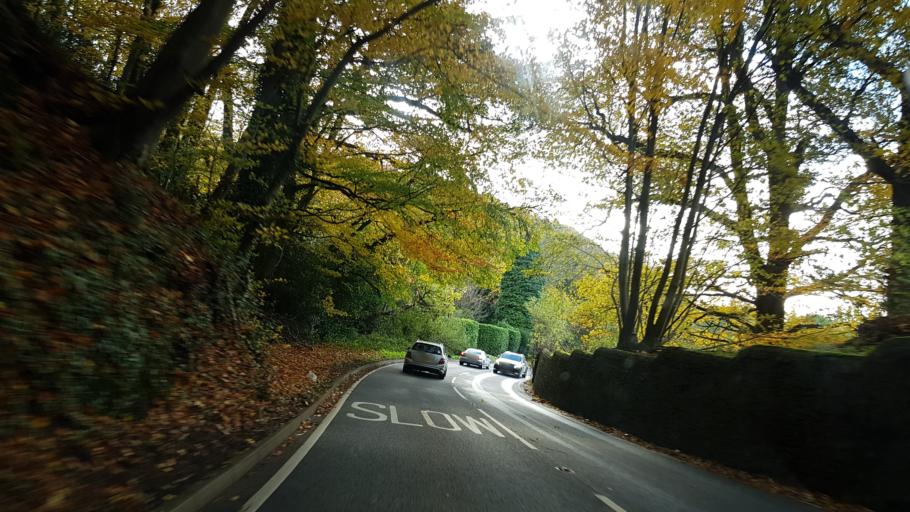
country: GB
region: England
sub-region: Surrey
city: Milford
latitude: 51.1385
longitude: -0.6727
